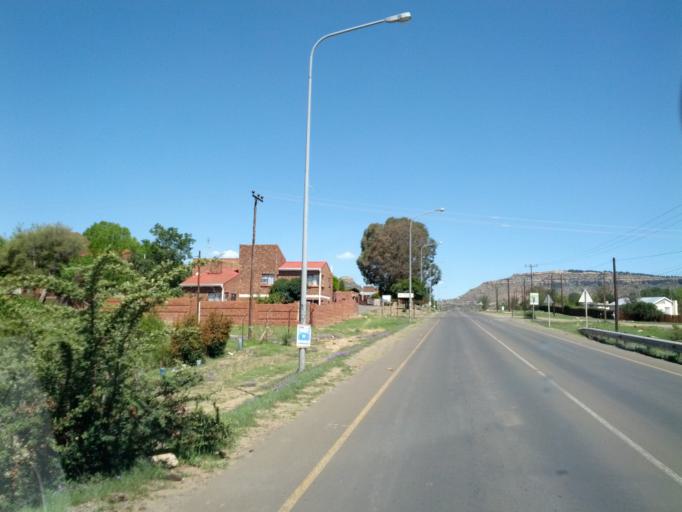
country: LS
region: Maseru
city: Maseru
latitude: -29.3086
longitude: 27.4654
